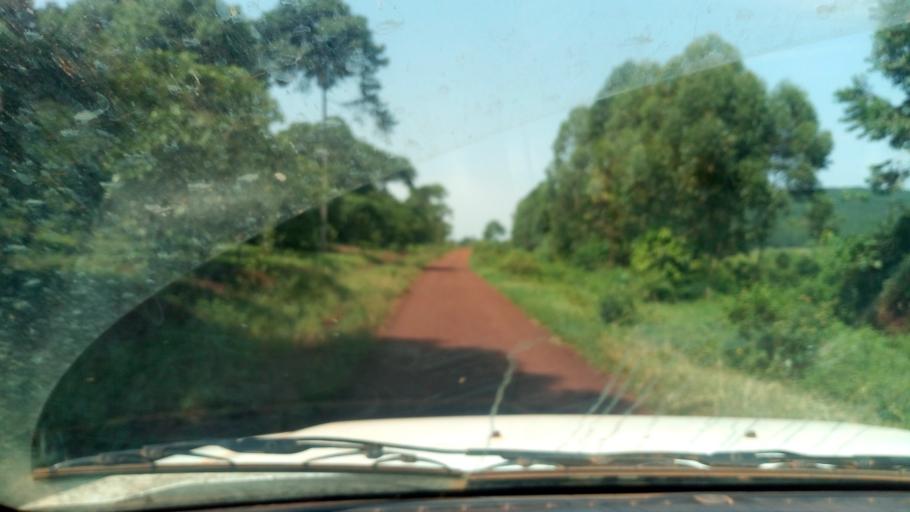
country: UG
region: Western Region
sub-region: Masindi District
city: Masindi
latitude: 1.6517
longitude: 31.8072
